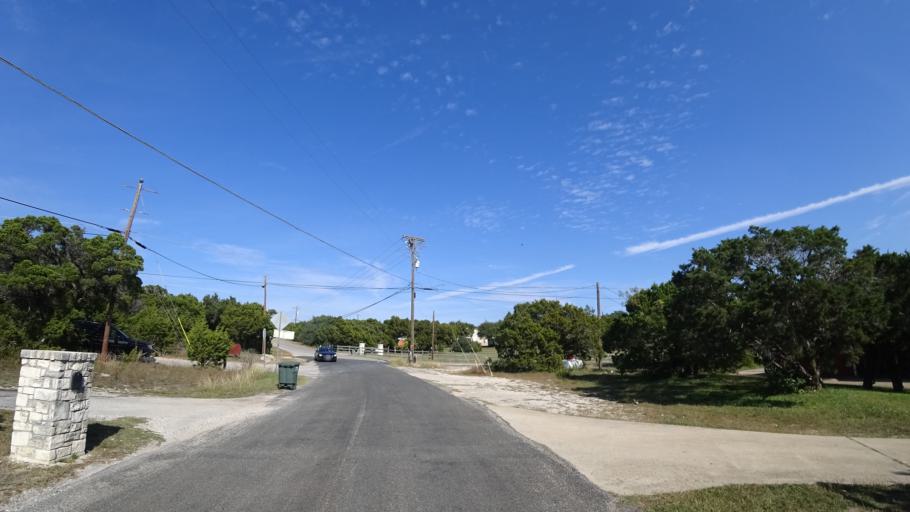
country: US
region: Texas
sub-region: Travis County
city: Barton Creek
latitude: 30.2302
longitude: -97.9128
